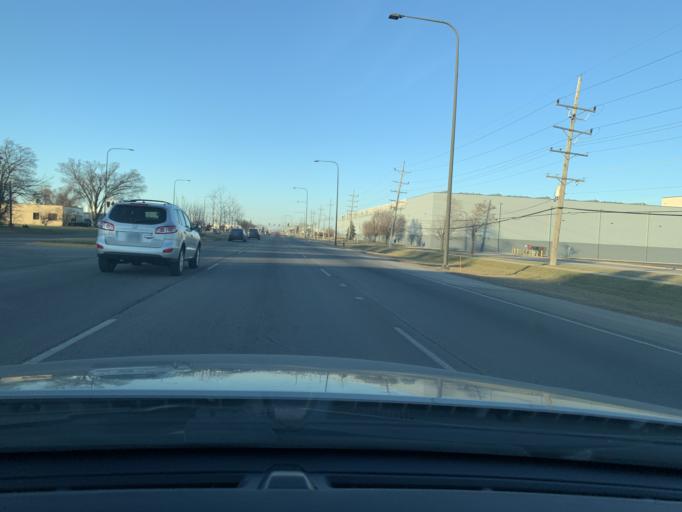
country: US
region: Illinois
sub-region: Cook County
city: Elk Grove Village
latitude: 41.9916
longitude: -87.9590
